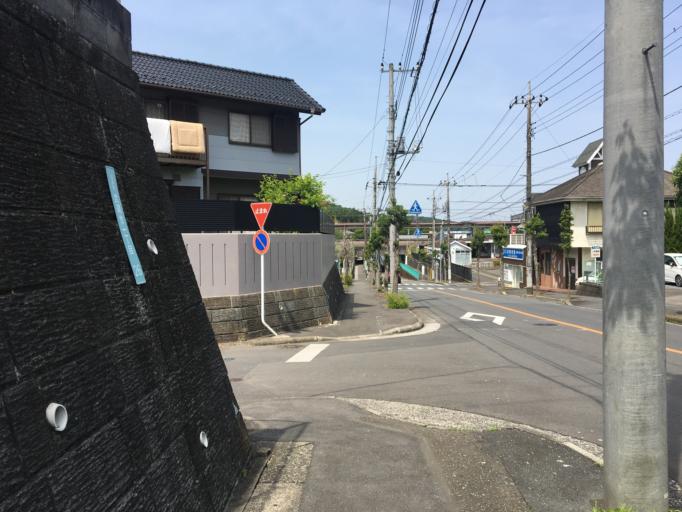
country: JP
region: Saitama
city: Hanno
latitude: 35.8808
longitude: 139.3036
